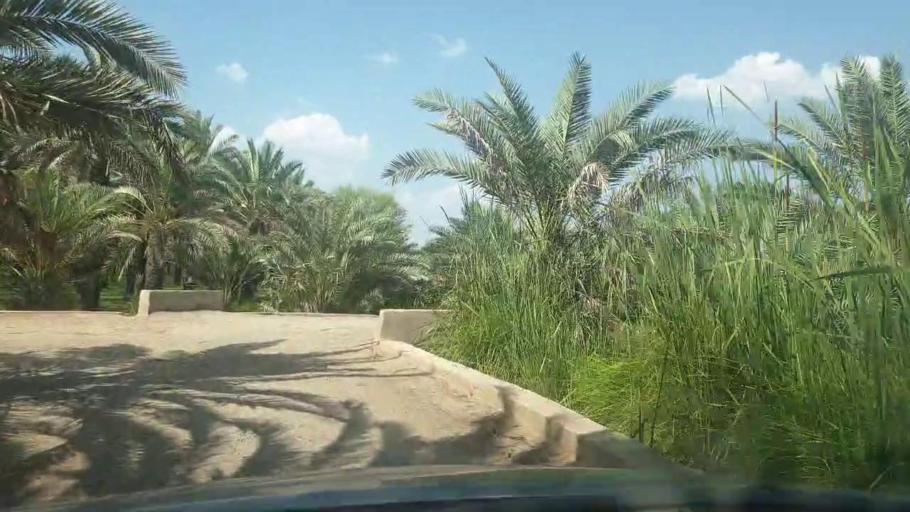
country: PK
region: Sindh
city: Khairpur
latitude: 27.5555
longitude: 68.8010
